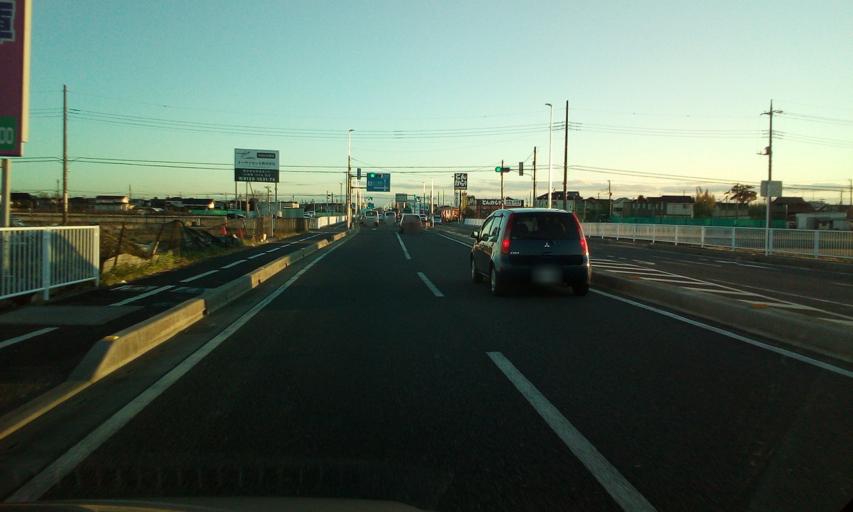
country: JP
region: Saitama
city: Yoshikawa
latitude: 35.8561
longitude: 139.8501
